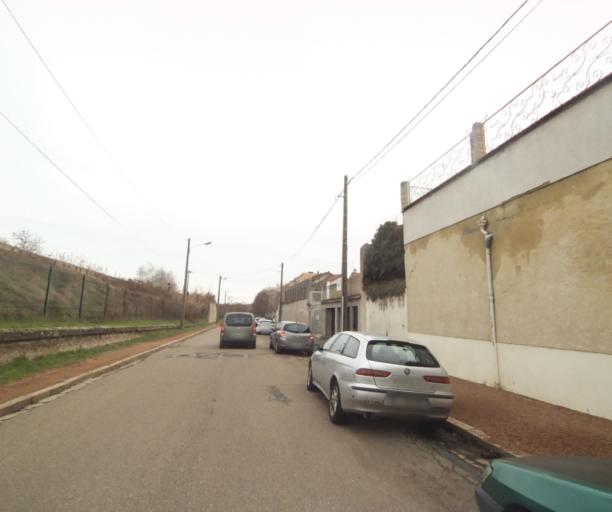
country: FR
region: Rhone-Alpes
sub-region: Departement de la Loire
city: Roanne
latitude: 46.0296
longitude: 4.0716
